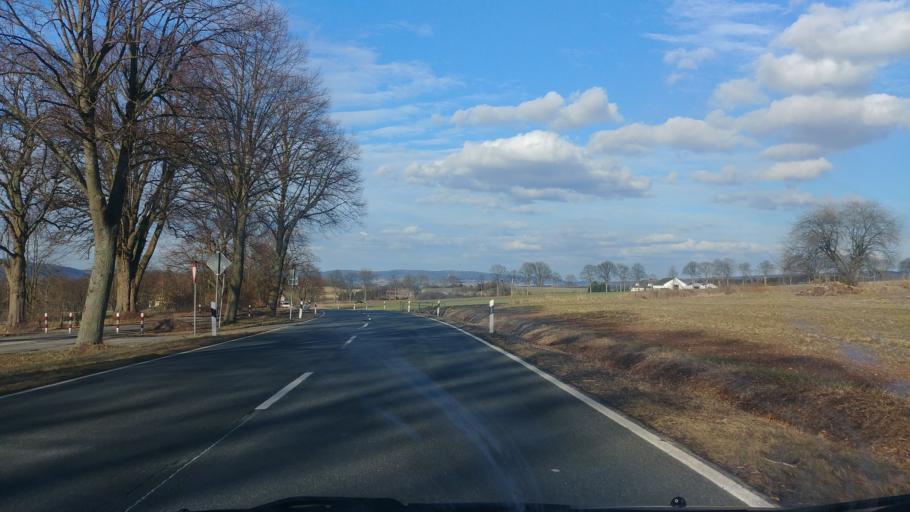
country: DE
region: Lower Saxony
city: Holzminden
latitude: 51.7945
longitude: 9.4495
